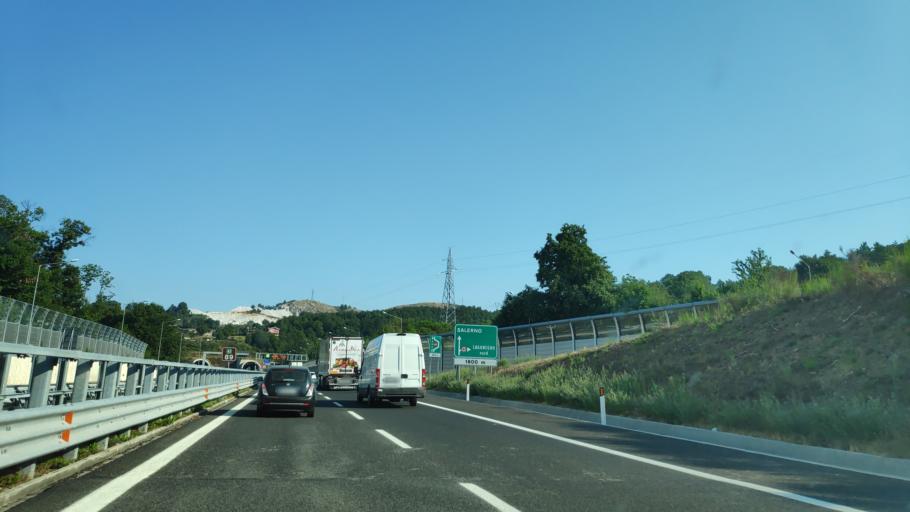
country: IT
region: Basilicate
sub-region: Provincia di Potenza
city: Lagonegro
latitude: 40.1352
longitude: 15.7605
